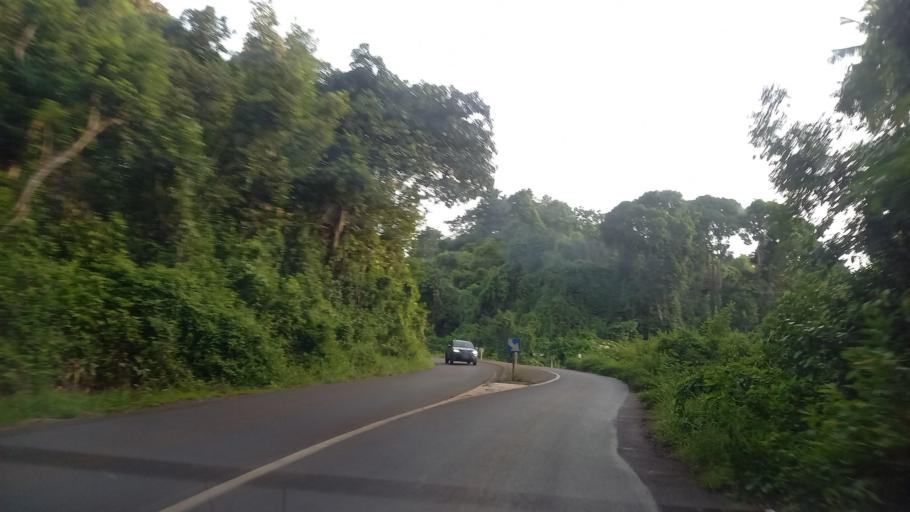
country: YT
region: Bandraboua
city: Bandraboua
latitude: -12.7351
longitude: 45.1189
